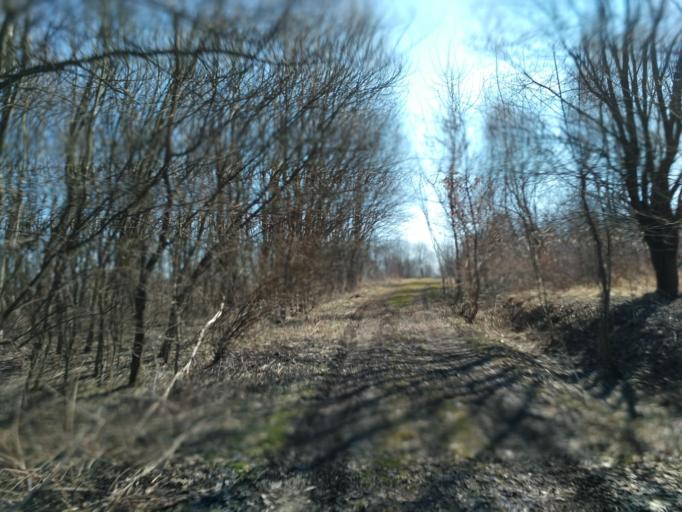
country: PL
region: Subcarpathian Voivodeship
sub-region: Powiat brzozowski
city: Domaradz
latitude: 49.7979
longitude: 21.9690
